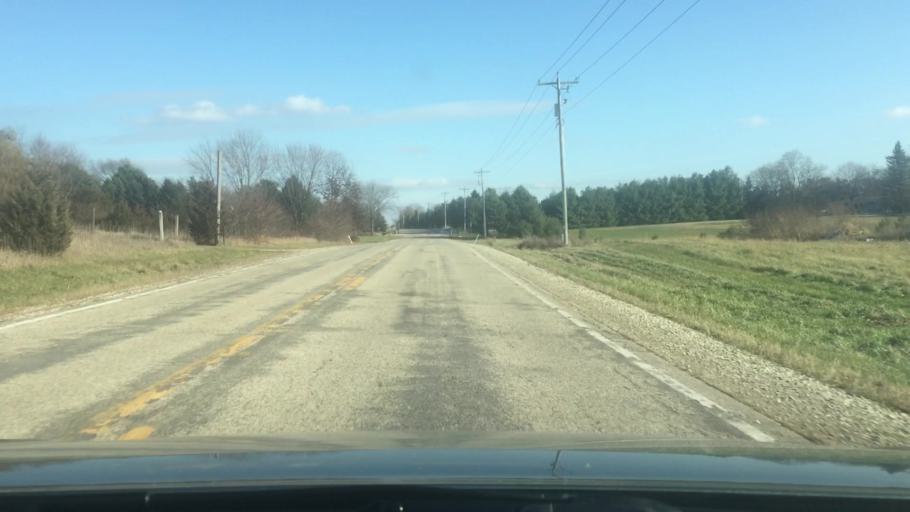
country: US
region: Wisconsin
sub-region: Jefferson County
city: Palmyra
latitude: 42.9330
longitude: -88.5789
